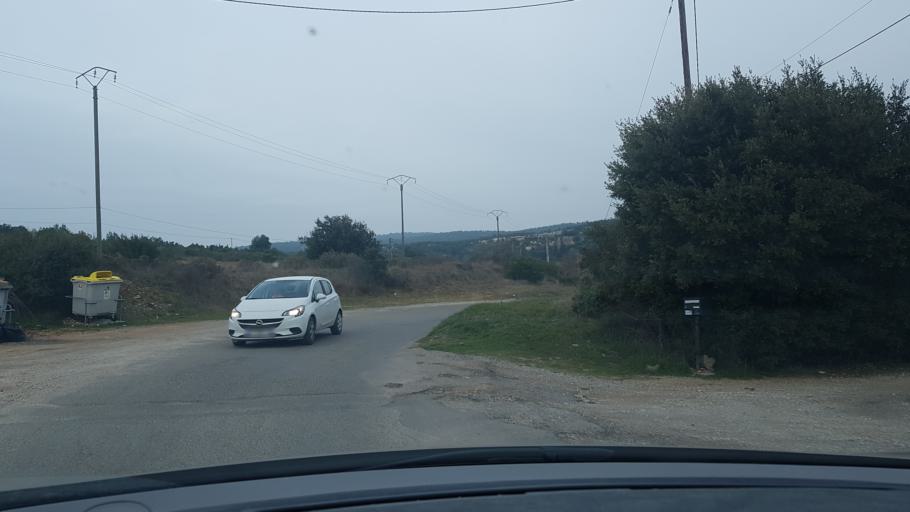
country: FR
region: Provence-Alpes-Cote d'Azur
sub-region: Departement des Bouches-du-Rhone
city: Meyreuil
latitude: 43.4824
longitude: 5.4783
